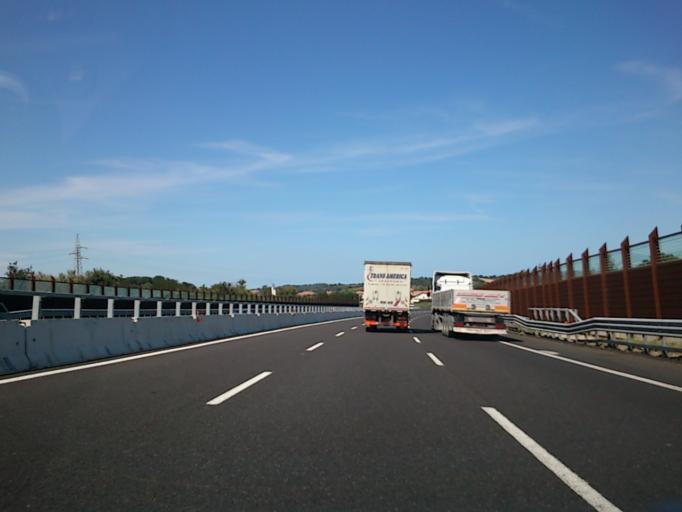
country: IT
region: The Marches
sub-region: Provincia di Pesaro e Urbino
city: Rosciano
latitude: 43.8236
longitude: 12.9990
